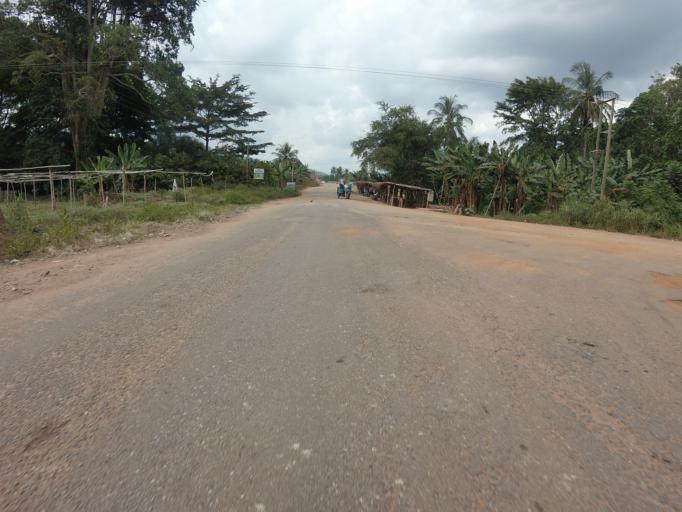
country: GH
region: Volta
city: Ho
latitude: 6.6699
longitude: 0.3531
